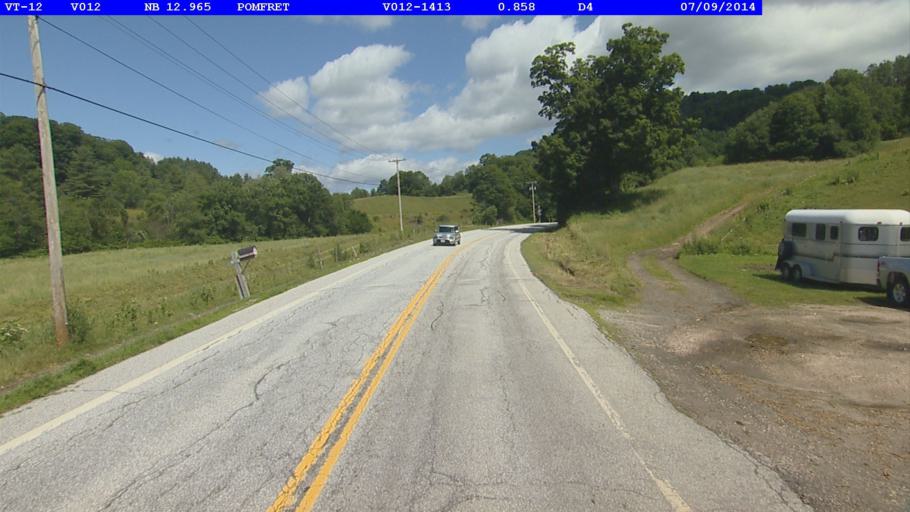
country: US
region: Vermont
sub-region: Windsor County
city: Woodstock
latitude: 43.6682
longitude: -72.5764
